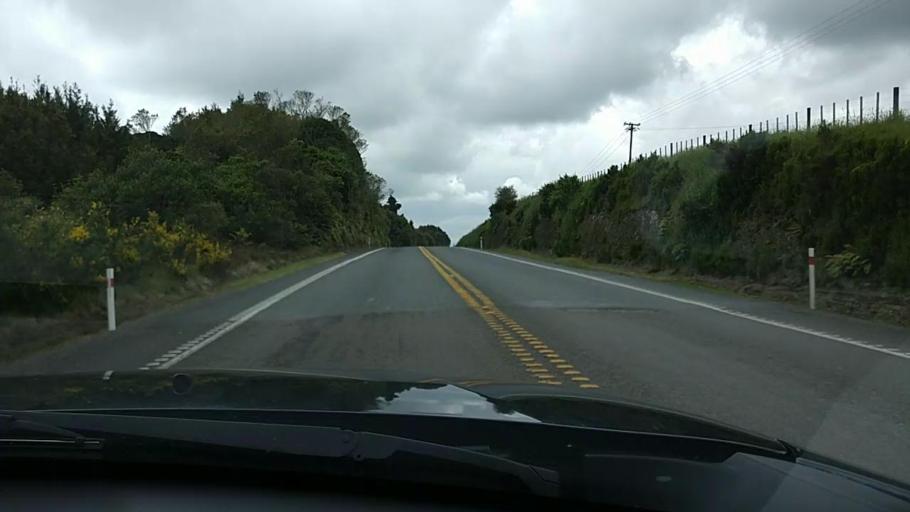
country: NZ
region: Bay of Plenty
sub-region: Rotorua District
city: Rotorua
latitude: -38.0661
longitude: 176.1046
